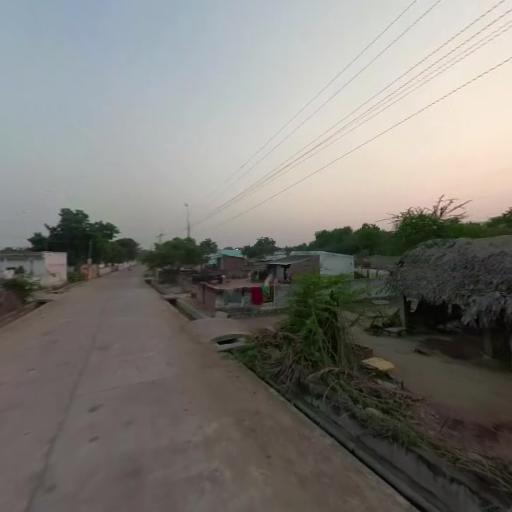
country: IN
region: Telangana
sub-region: Nalgonda
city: Suriapet
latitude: 17.1075
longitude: 79.5284
